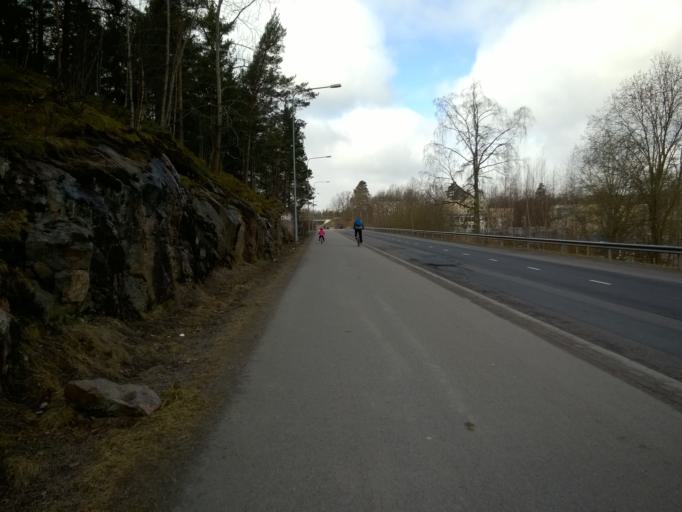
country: FI
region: Uusimaa
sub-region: Helsinki
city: Helsinki
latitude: 60.2310
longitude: 24.9799
